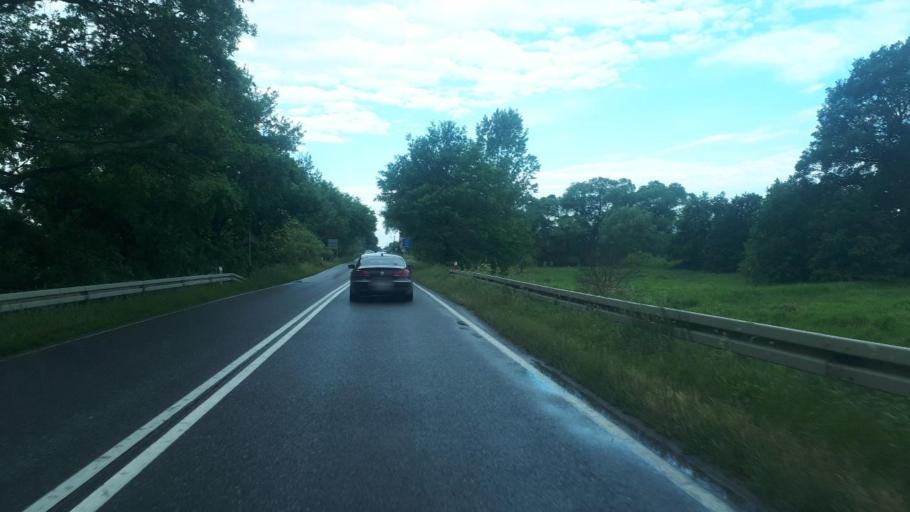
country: PL
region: Silesian Voivodeship
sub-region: Powiat pszczynski
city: Gora
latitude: 49.9734
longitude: 19.1134
